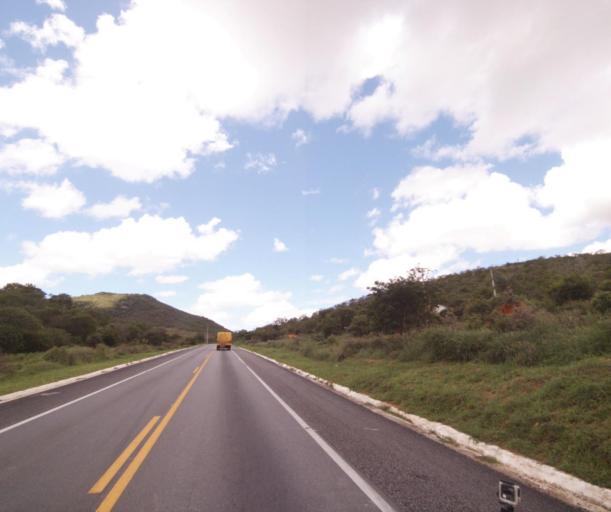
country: BR
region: Bahia
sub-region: Pocoes
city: Pocoes
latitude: -14.3559
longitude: -40.3369
